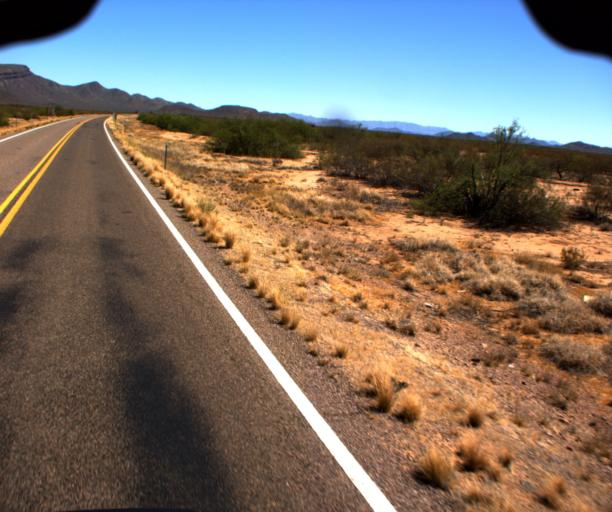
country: US
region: Arizona
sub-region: Yavapai County
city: Congress
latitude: 33.9813
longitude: -113.1394
